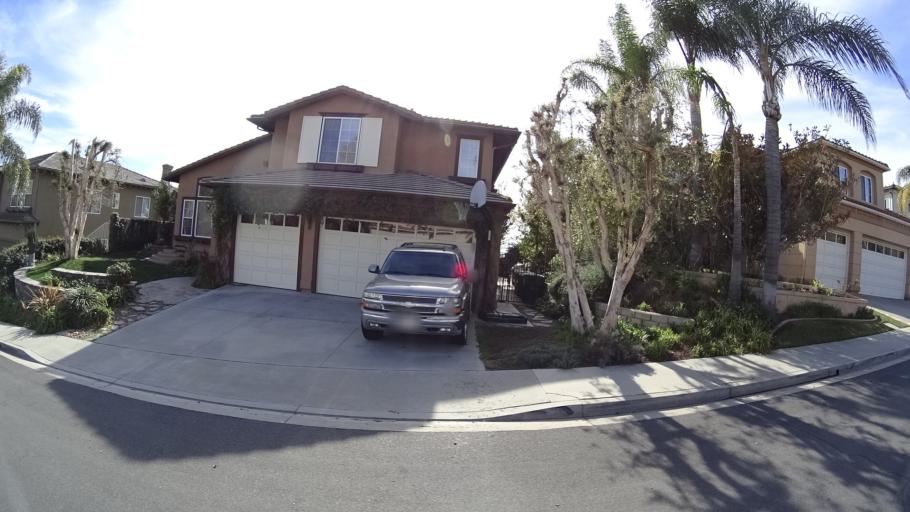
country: US
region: California
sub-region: Orange County
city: Portola Hills
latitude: 33.6771
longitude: -117.6377
